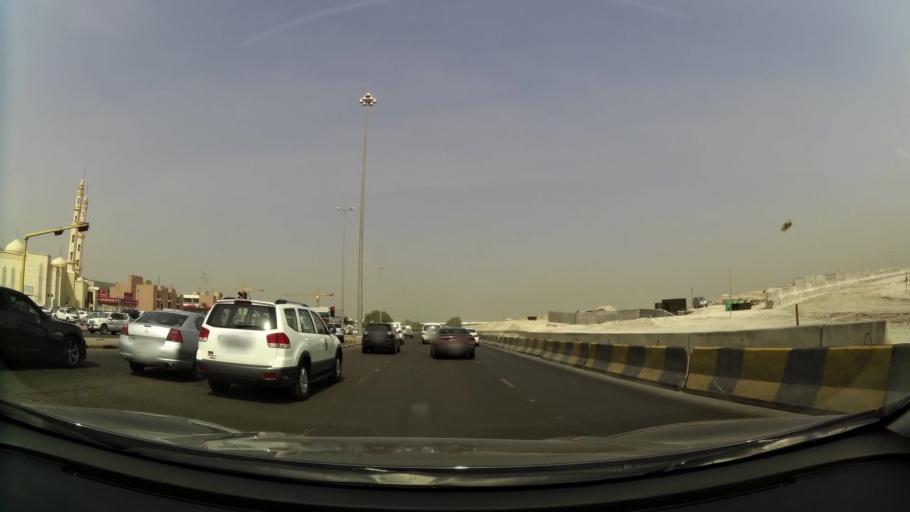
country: KW
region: Al Asimah
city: Ar Rabiyah
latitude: 29.2699
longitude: 47.9077
